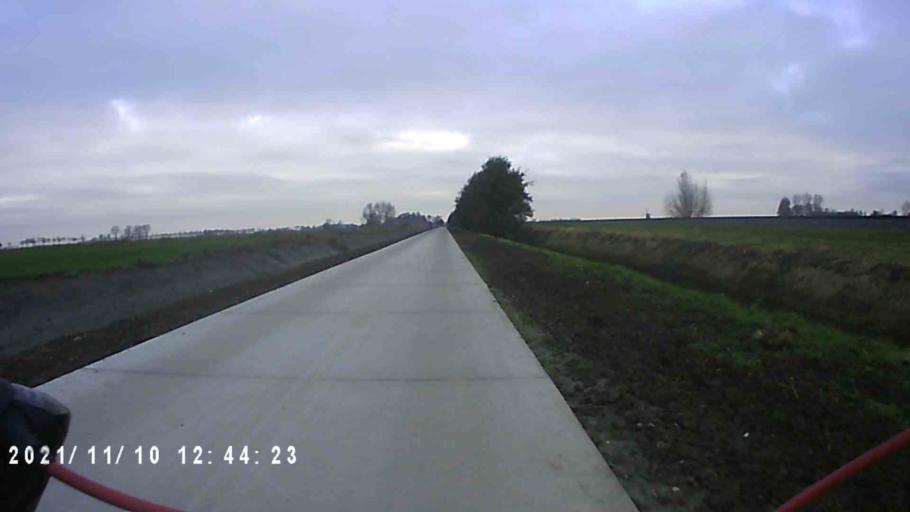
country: NL
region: Groningen
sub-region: Gemeente Groningen
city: Korrewegwijk
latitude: 53.2571
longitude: 6.5495
